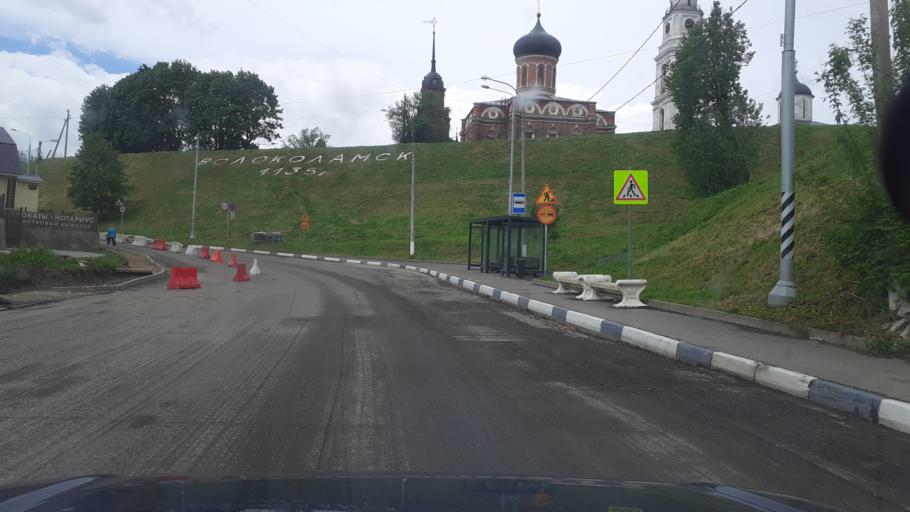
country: RU
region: Moskovskaya
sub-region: Volokolamskiy Rayon
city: Volokolamsk
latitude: 56.0366
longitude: 35.9572
